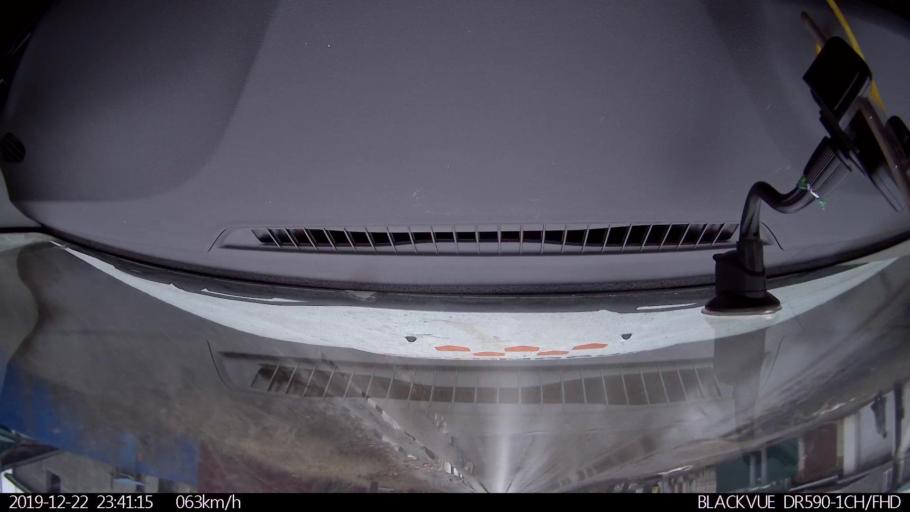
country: RU
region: Nizjnij Novgorod
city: Nizhniy Novgorod
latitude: 56.2837
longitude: 43.9108
